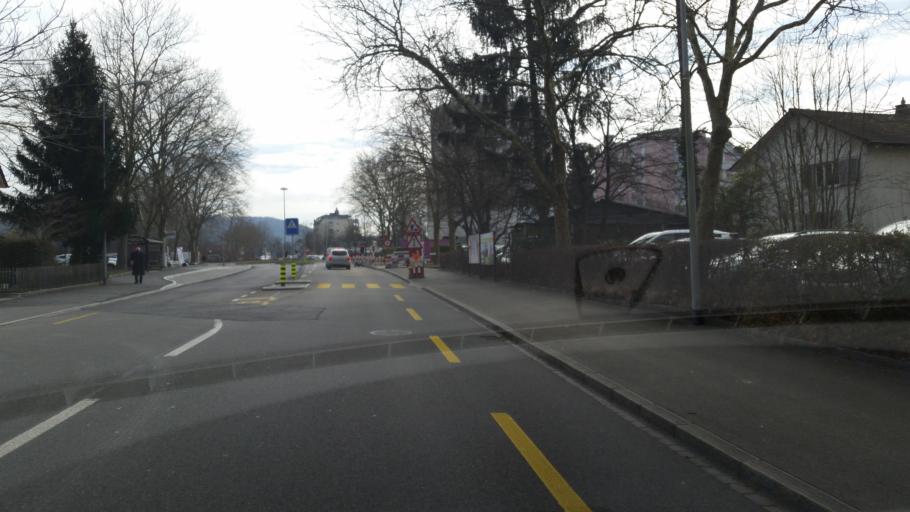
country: CH
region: Aargau
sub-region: Bezirk Baden
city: Neuenhof
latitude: 47.4595
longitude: 8.3334
